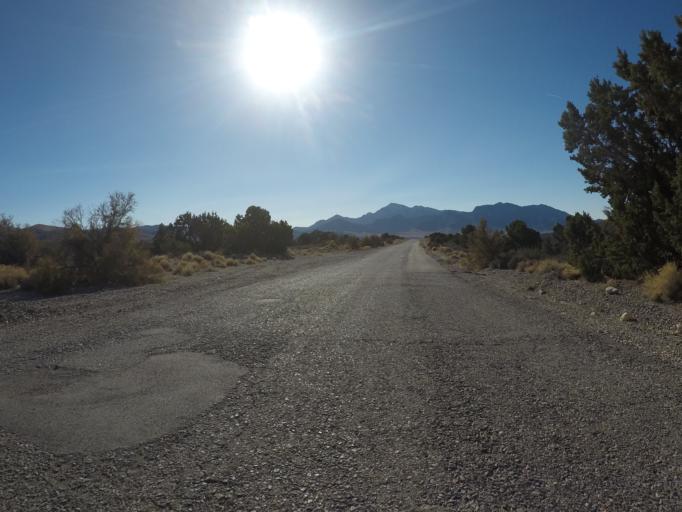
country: US
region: Nevada
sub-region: Clark County
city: Summerlin South
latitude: 36.0747
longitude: -115.5638
